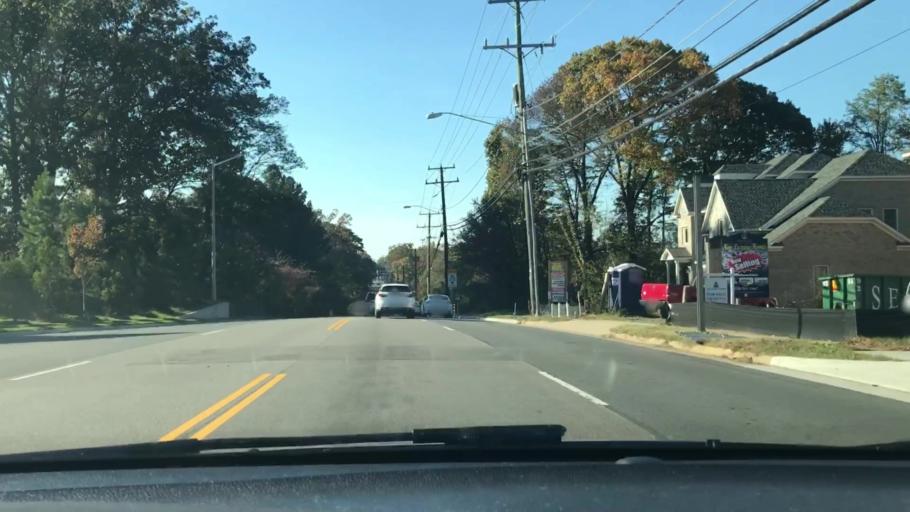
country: US
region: Virginia
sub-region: Fairfax County
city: Annandale
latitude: 38.8507
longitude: -77.2119
